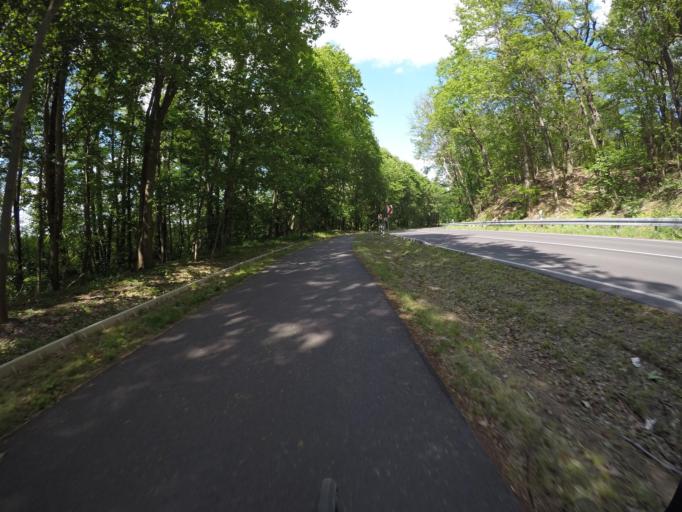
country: DE
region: Brandenburg
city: Potsdam
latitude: 52.3764
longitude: 13.0389
